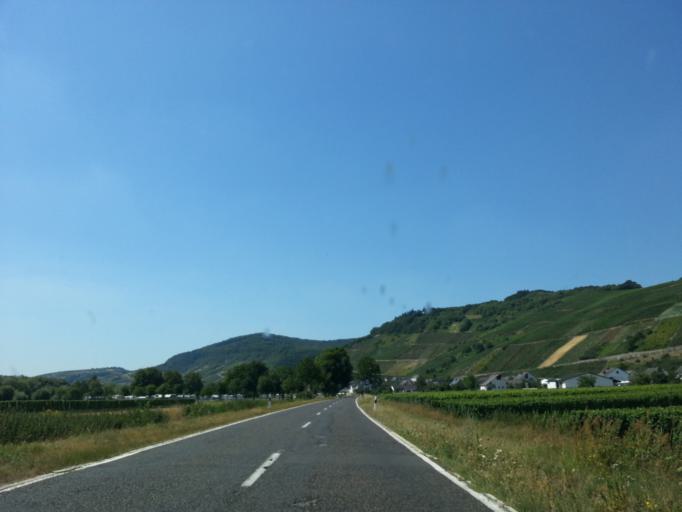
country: DE
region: Rheinland-Pfalz
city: Kesten
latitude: 49.9052
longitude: 6.9648
